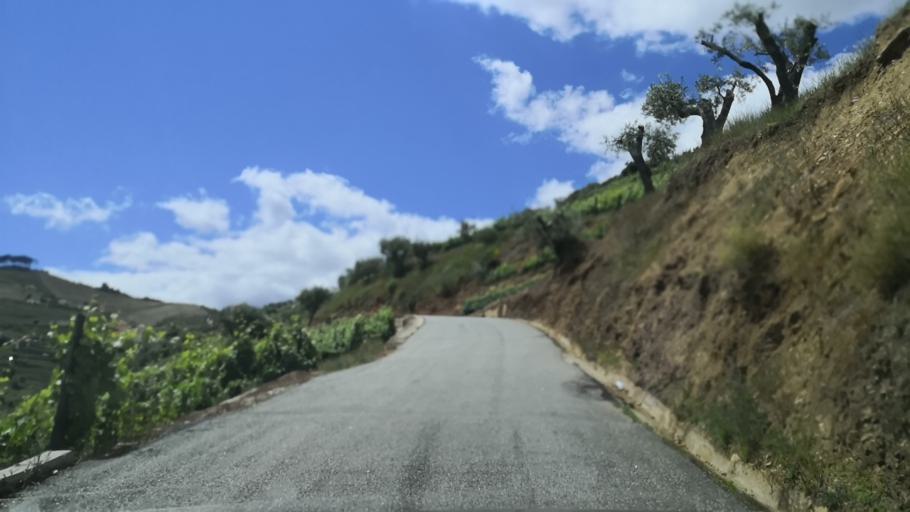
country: PT
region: Vila Real
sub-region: Santa Marta de Penaguiao
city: Santa Marta de Penaguiao
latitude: 41.2280
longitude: -7.7828
